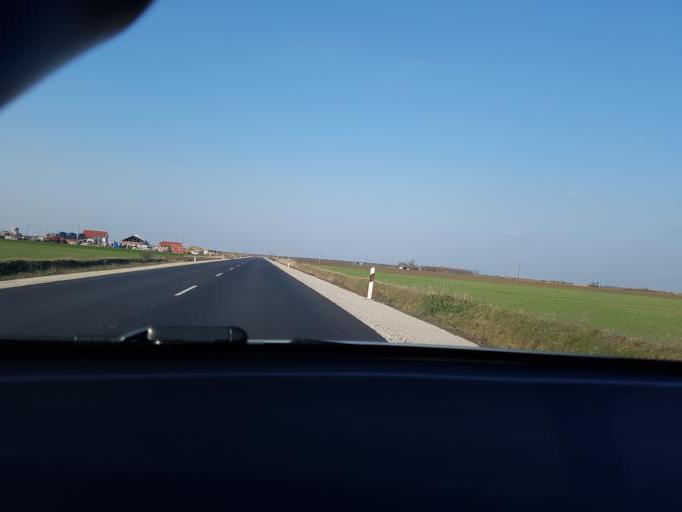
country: RO
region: Arad
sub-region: Comuna Nadlac
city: Nadlac
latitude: 46.2013
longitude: 20.7162
